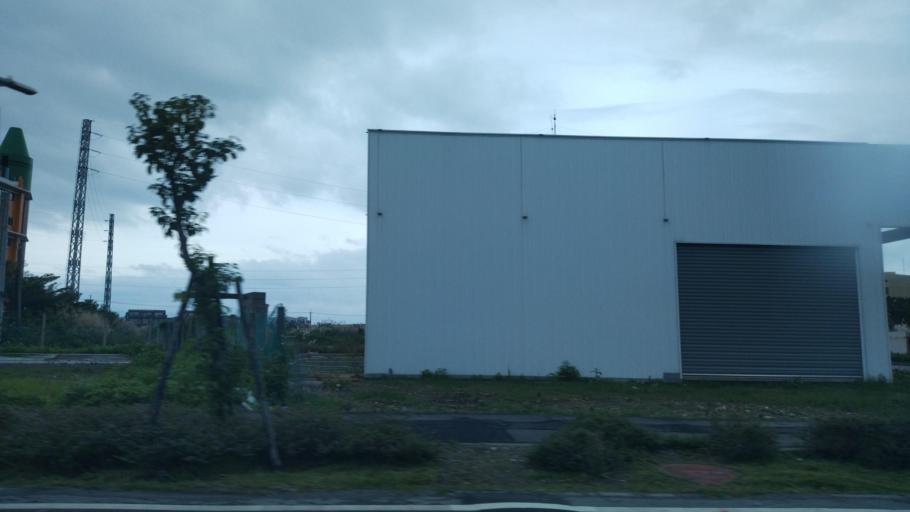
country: TW
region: Taiwan
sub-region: Yilan
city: Yilan
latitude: 24.6155
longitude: 121.8284
